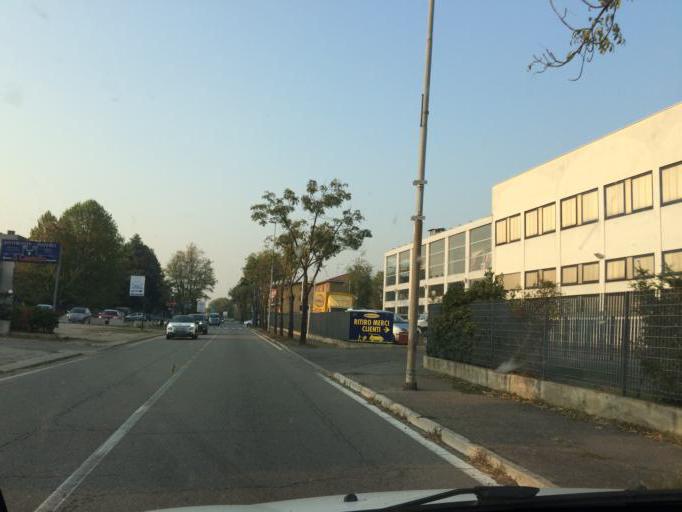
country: IT
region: Lombardy
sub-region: Provincia di Varese
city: Castellanza
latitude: 45.5972
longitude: 8.8962
